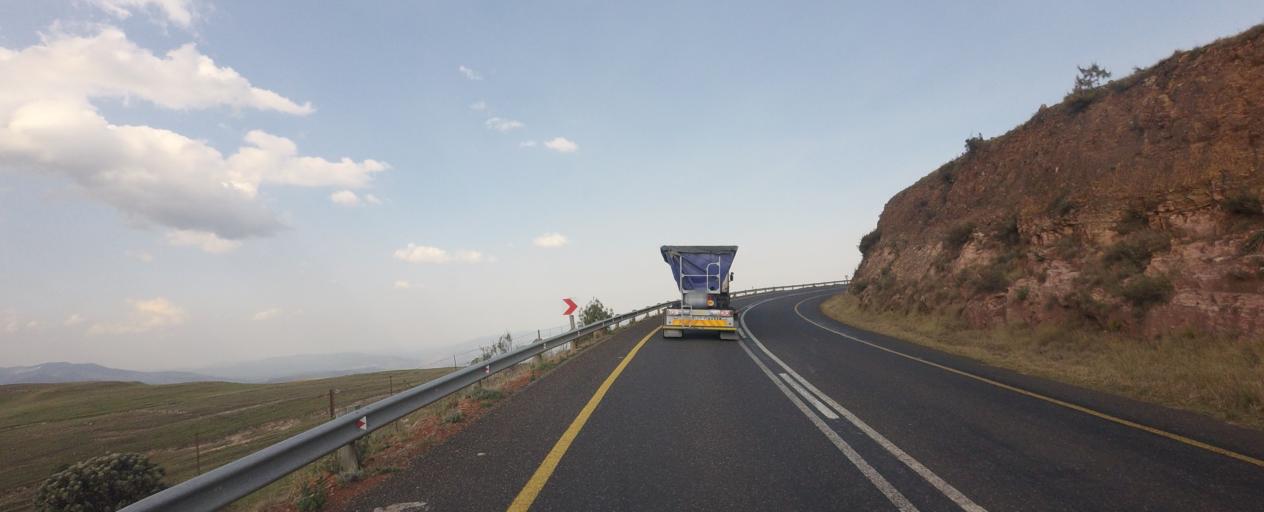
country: ZA
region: Mpumalanga
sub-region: Ehlanzeni District
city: Lydenburg
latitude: -25.1415
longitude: 30.6212
